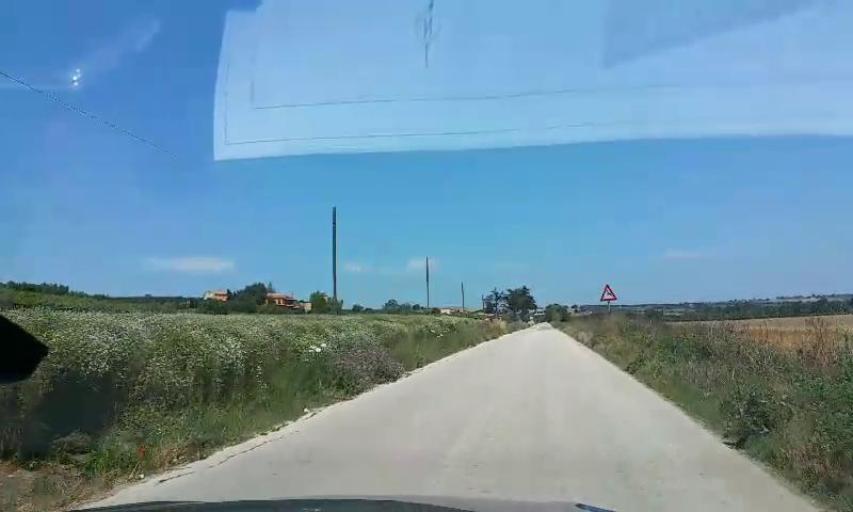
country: IT
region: Molise
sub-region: Provincia di Campobasso
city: San Giacomo degli Schiavoni
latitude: 41.9652
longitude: 14.9004
